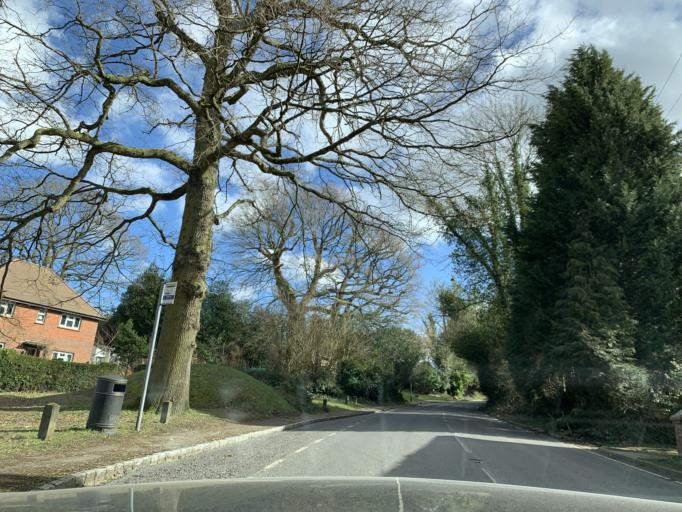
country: GB
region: England
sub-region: West Sussex
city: Crawley Down
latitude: 51.1076
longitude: -0.0870
